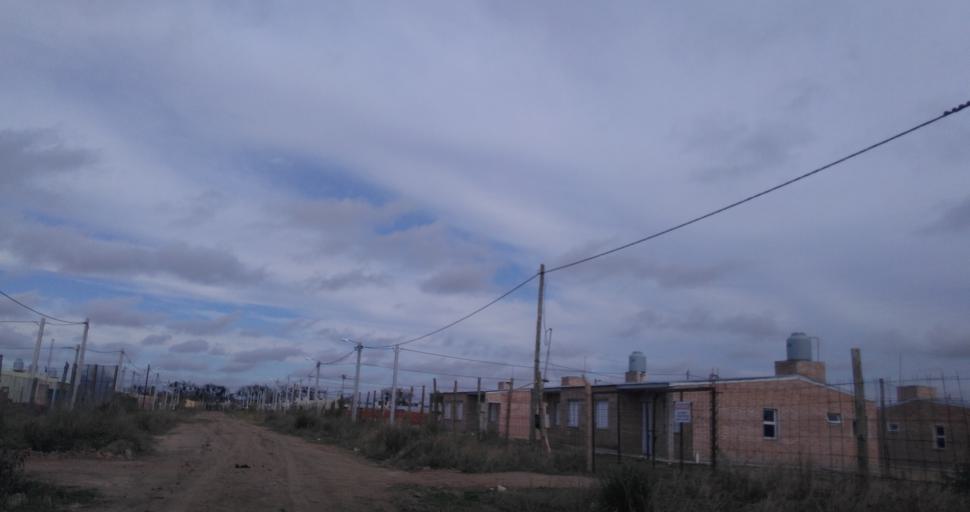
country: AR
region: Chaco
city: Fontana
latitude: -27.3947
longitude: -58.9880
